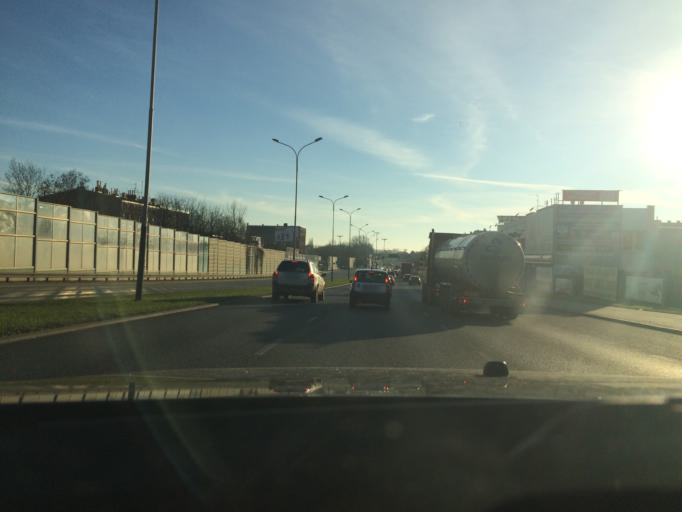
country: PL
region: Lodz Voivodeship
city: Lodz
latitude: 51.7393
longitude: 19.4422
